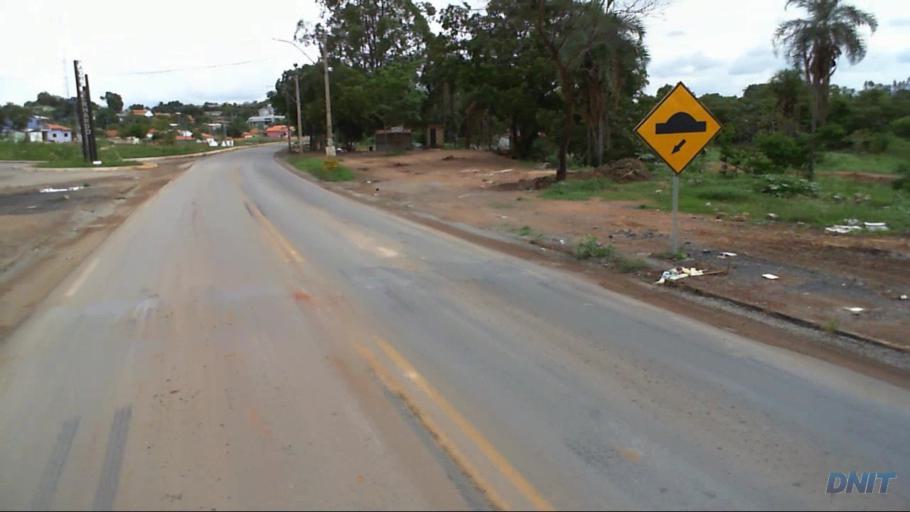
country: BR
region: Goias
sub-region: Padre Bernardo
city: Padre Bernardo
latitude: -15.1776
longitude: -48.2858
